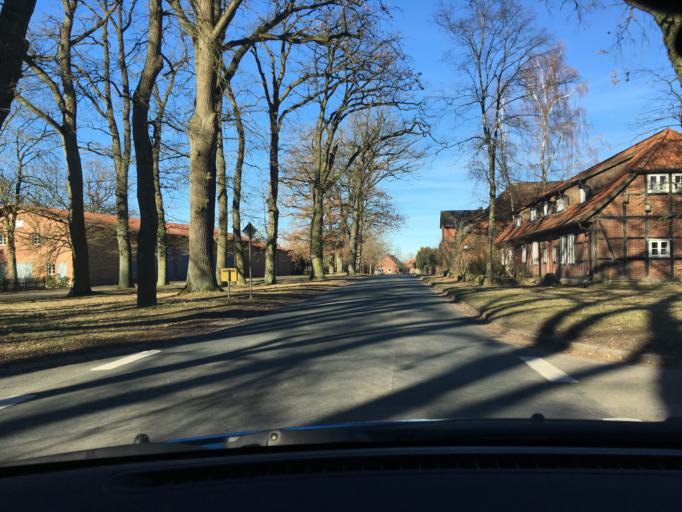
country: DE
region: Lower Saxony
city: Schwienau
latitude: 52.9792
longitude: 10.4451
